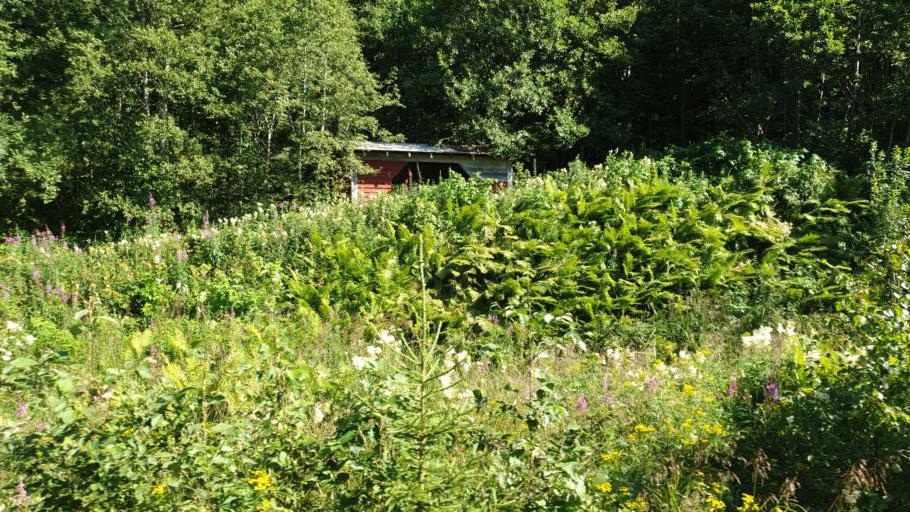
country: NO
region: Sor-Trondelag
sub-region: Orkdal
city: Orkanger
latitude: 63.1888
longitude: 9.7787
